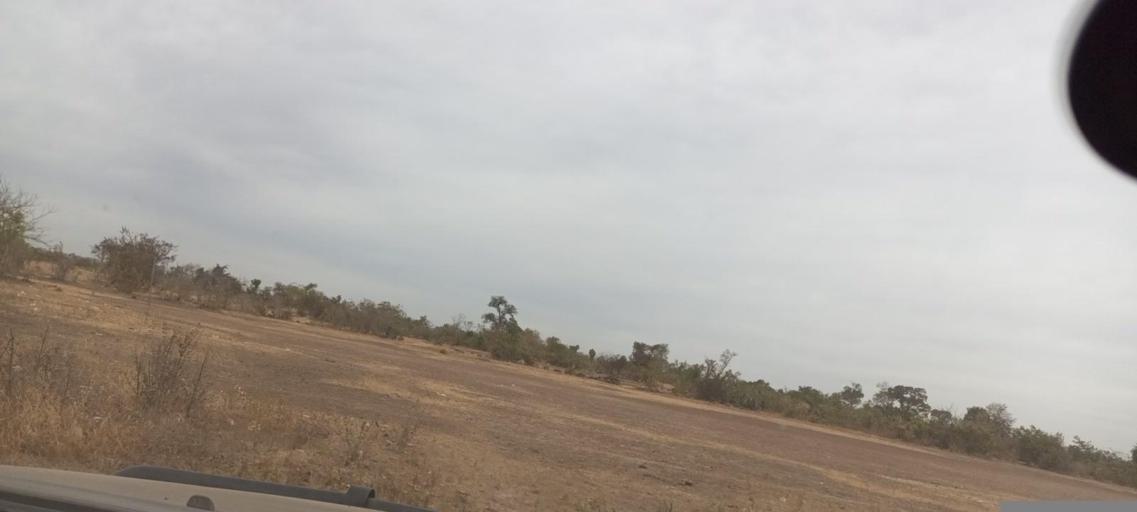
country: ML
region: Koulikoro
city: Kati
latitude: 12.7503
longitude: -8.3605
